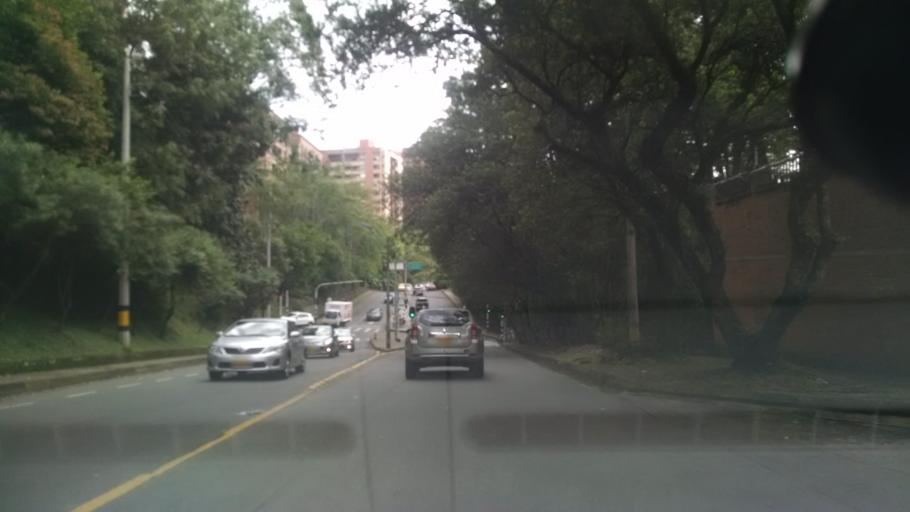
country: CO
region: Antioquia
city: Envigado
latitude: 6.1977
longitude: -75.5683
